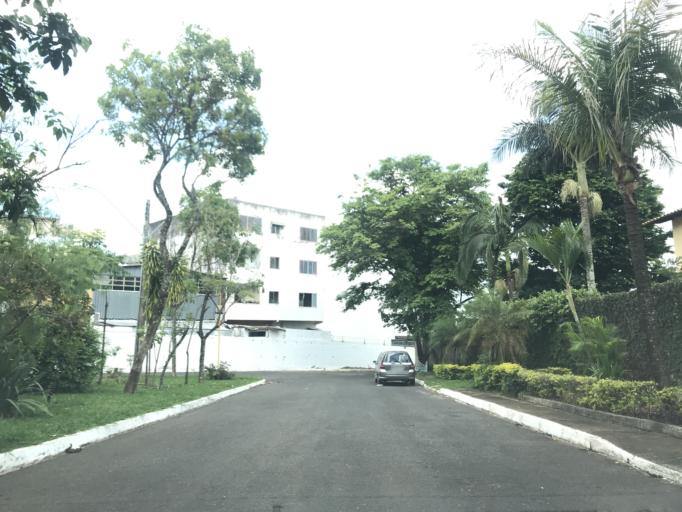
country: BR
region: Federal District
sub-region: Brasilia
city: Brasilia
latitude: -15.6818
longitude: -47.8331
